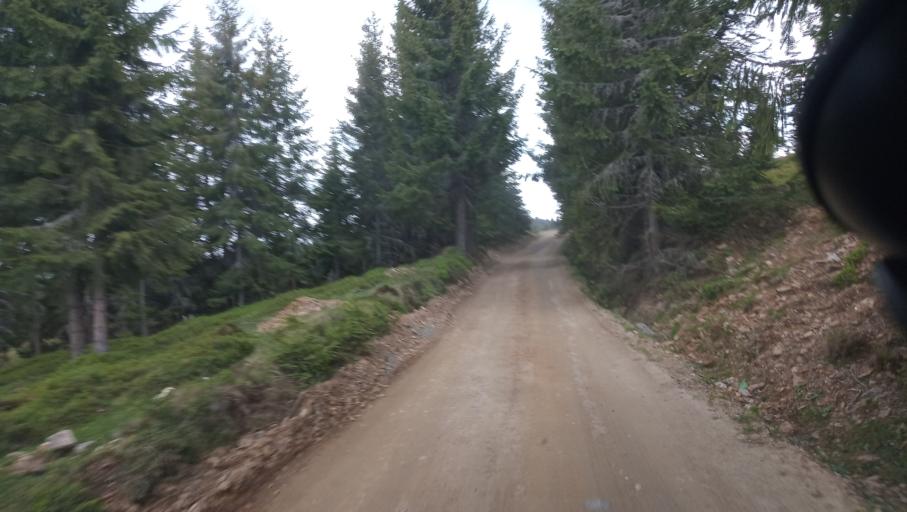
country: RO
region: Cluj
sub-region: Comuna Belis
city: Belis
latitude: 46.6313
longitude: 23.0442
